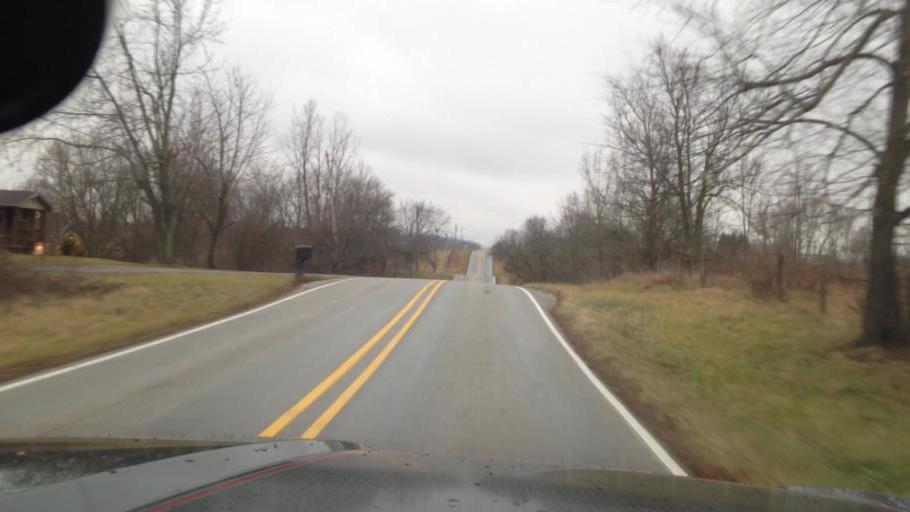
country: US
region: Ohio
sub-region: Preble County
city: New Paris
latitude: 39.9120
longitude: -84.8317
